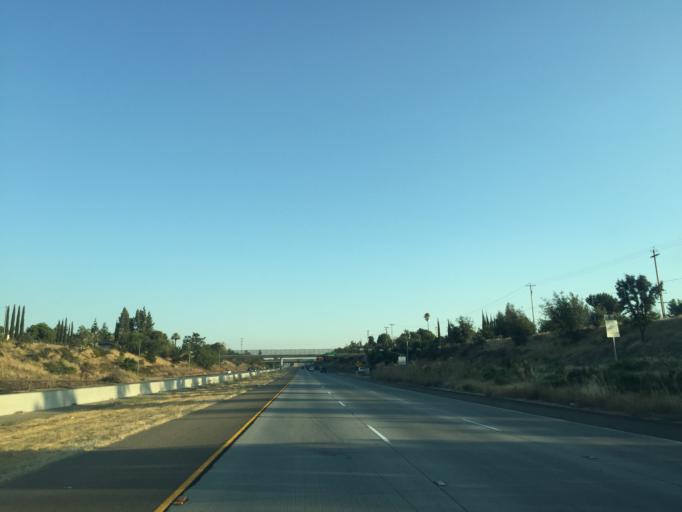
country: US
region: California
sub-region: Fresno County
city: Fresno
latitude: 36.7789
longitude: -119.7493
